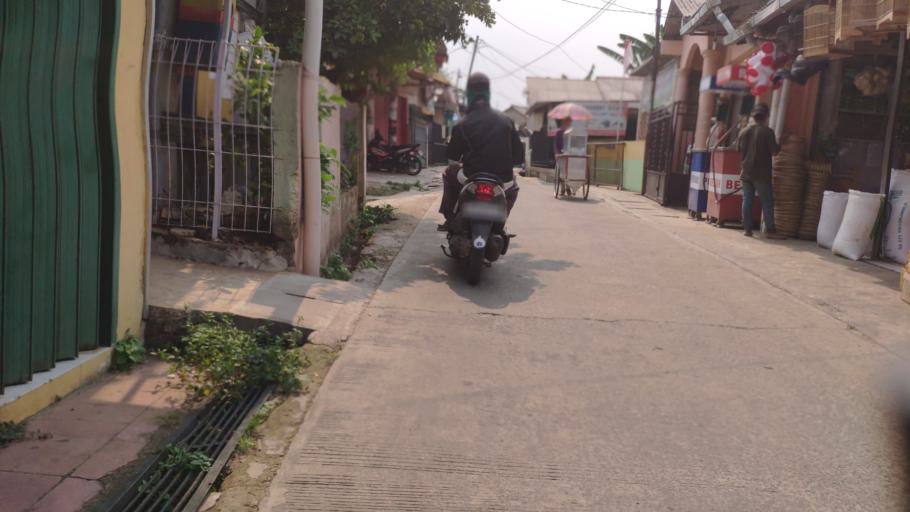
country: ID
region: West Java
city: Depok
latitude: -6.3832
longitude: 106.7976
